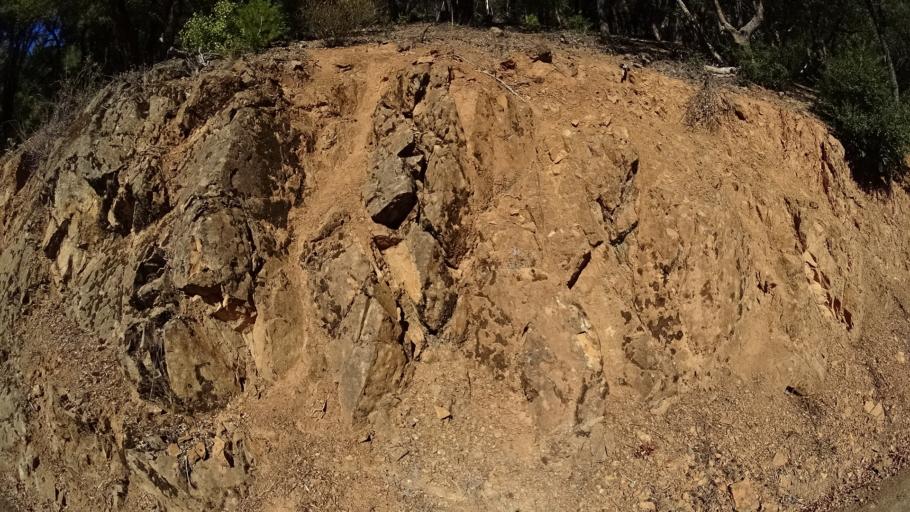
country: US
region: California
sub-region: Siskiyou County
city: Happy Camp
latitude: 41.2944
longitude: -123.1124
